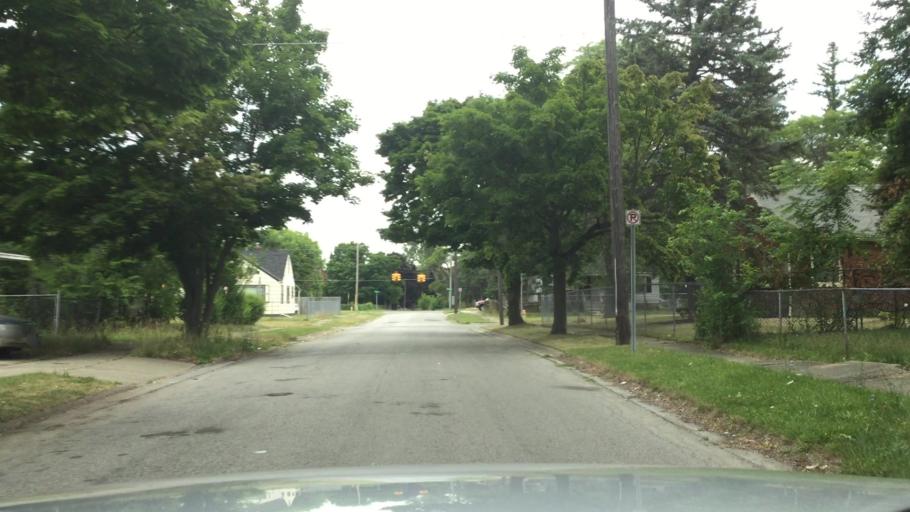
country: US
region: Michigan
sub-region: Genesee County
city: Beecher
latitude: 43.0596
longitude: -83.7099
